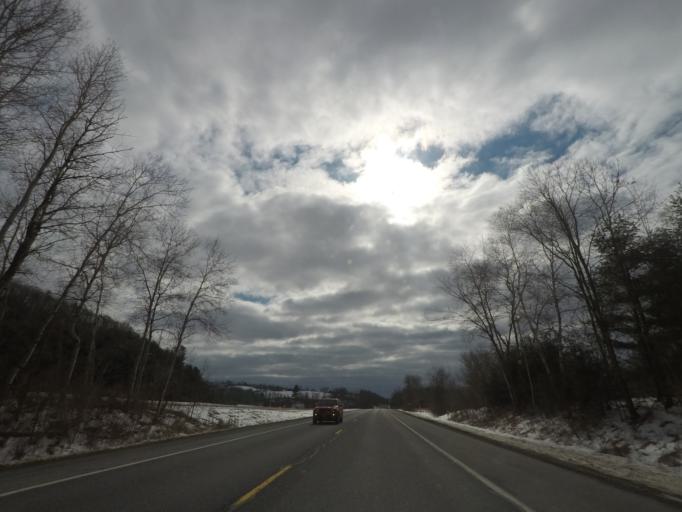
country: US
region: New York
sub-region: Washington County
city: Cambridge
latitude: 42.9871
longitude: -73.3755
